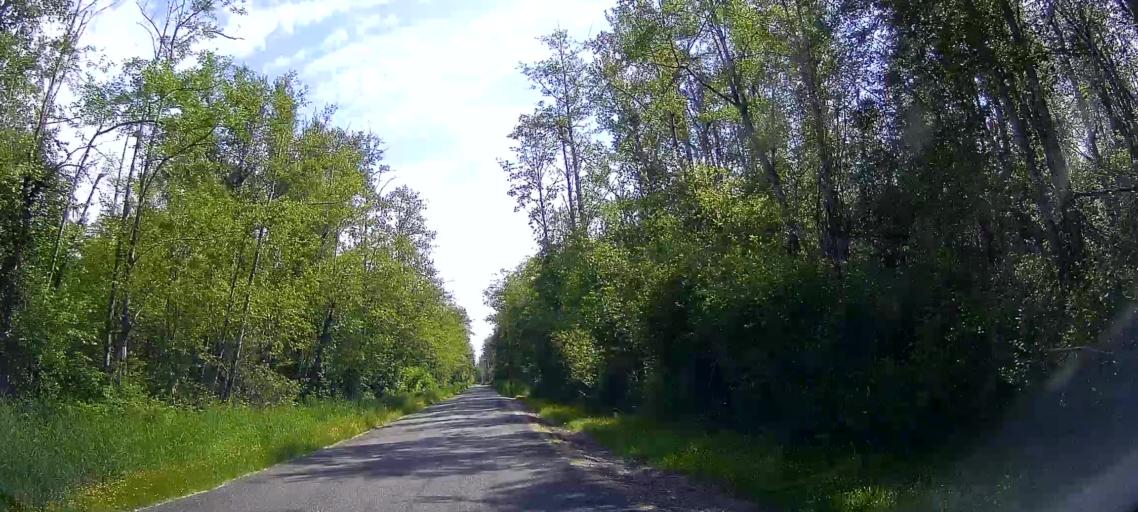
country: US
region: Washington
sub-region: Skagit County
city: Burlington
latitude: 48.5395
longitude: -122.3622
